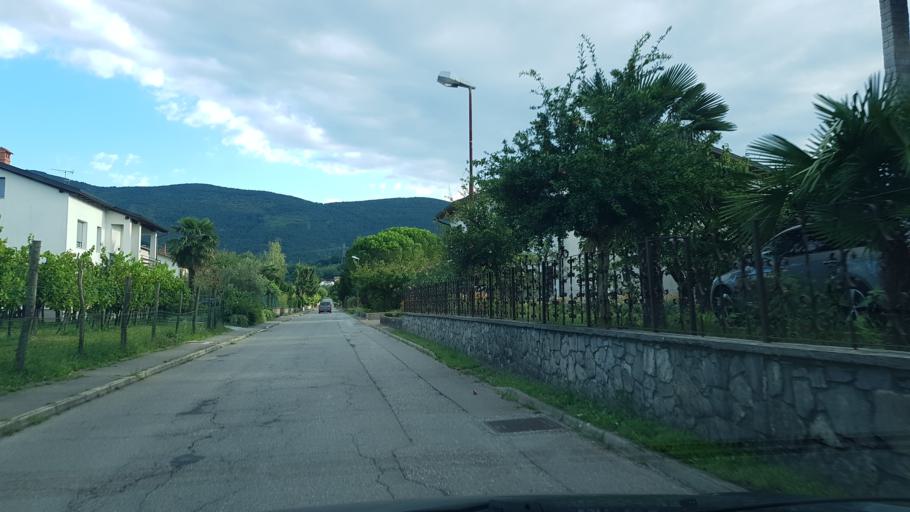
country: SI
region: Rence-Vogrsko
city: Rence
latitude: 45.8874
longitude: 13.6678
